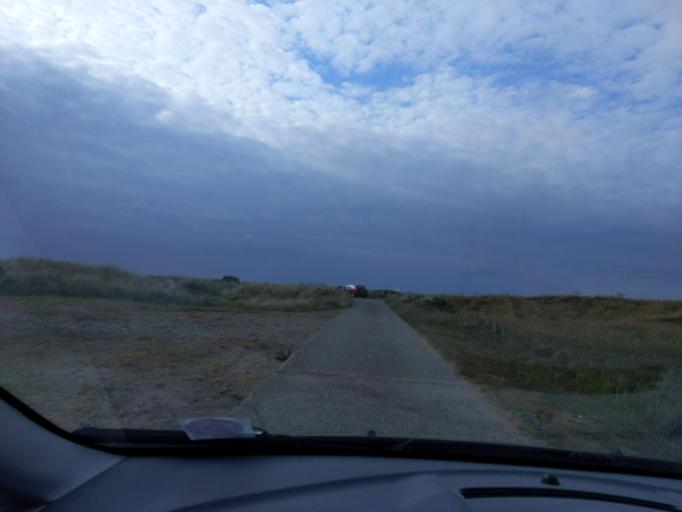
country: IM
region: Ramsey
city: Ramsey
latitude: 54.3986
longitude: -4.4453
